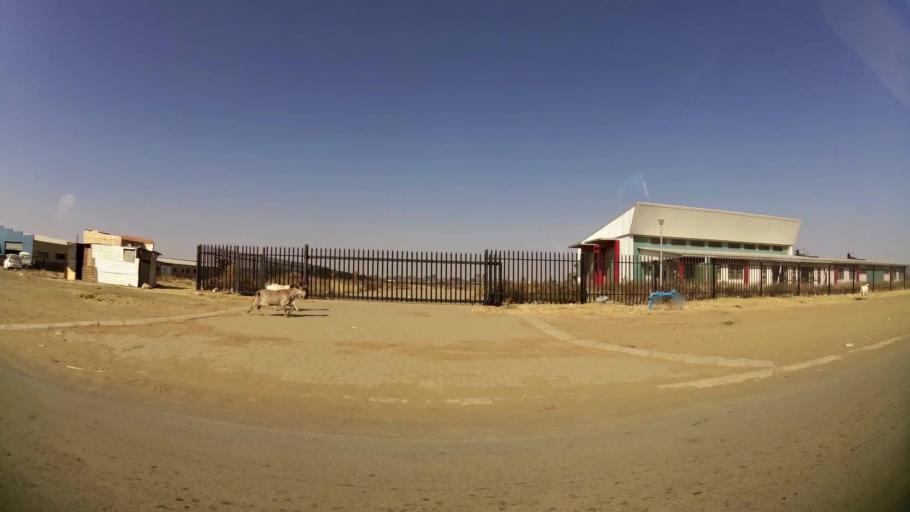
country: ZA
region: Orange Free State
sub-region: Mangaung Metropolitan Municipality
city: Bloemfontein
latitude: -29.1951
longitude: 26.2711
